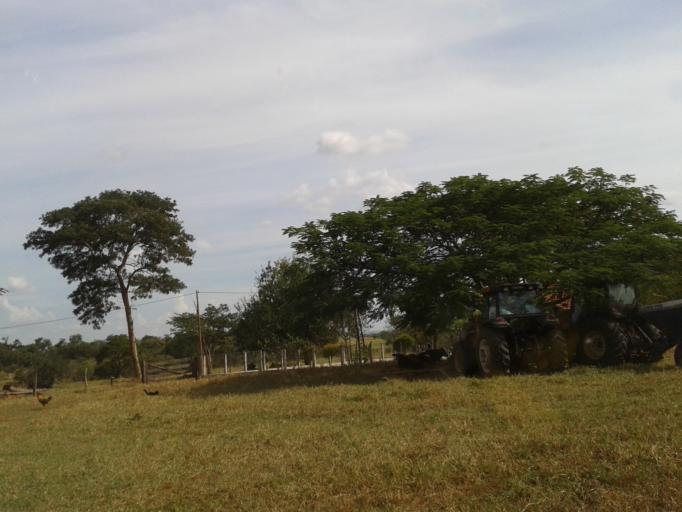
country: BR
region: Minas Gerais
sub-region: Campina Verde
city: Campina Verde
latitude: -19.5153
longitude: -49.5961
